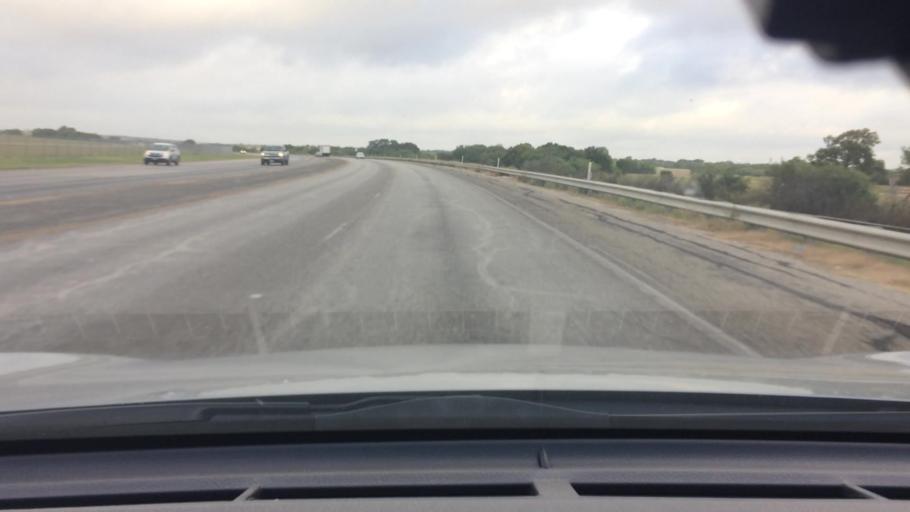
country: US
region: Texas
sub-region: Bexar County
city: Universal City
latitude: 29.5416
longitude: -98.2934
